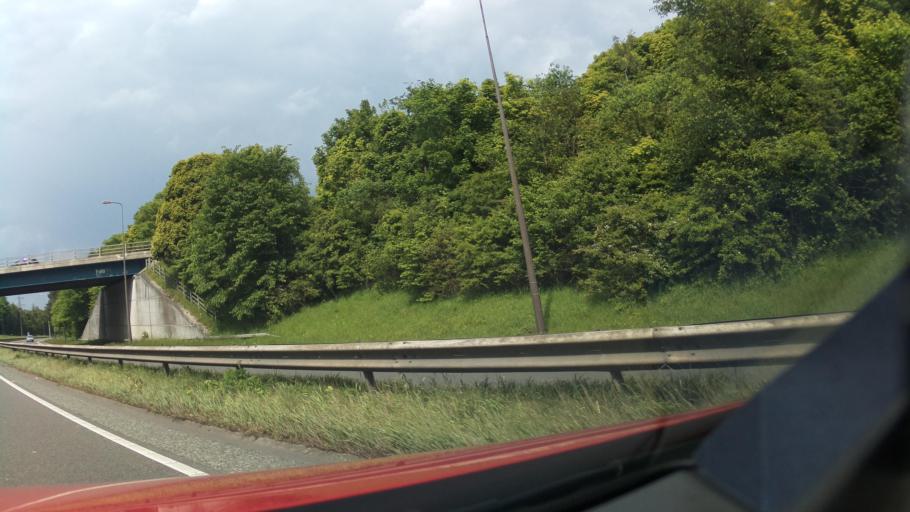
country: GB
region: England
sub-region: County Durham
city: Wingate
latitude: 54.7370
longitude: -1.3634
